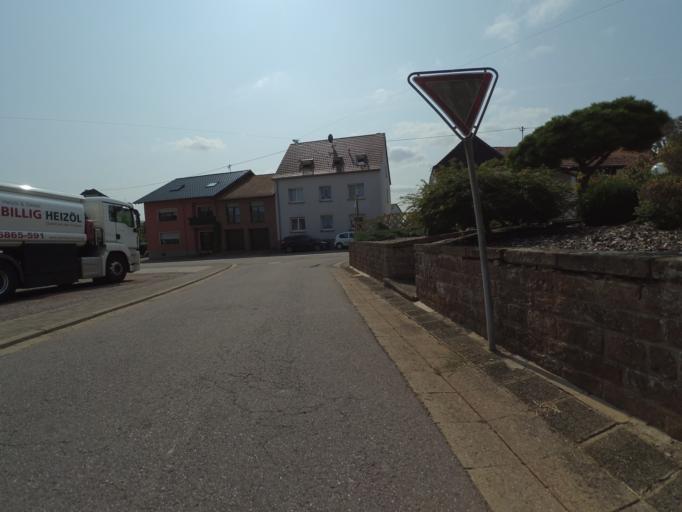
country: DE
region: Saarland
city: Weiten
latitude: 49.5333
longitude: 6.5394
